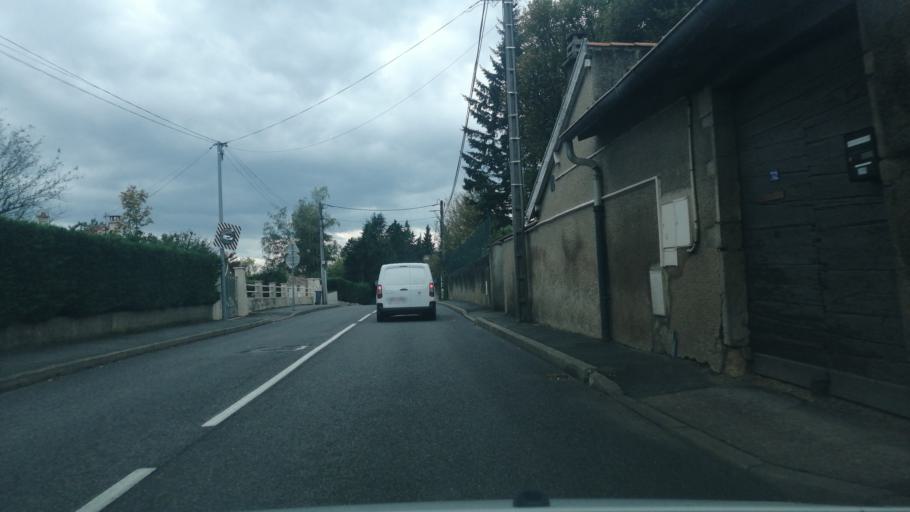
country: FR
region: Rhone-Alpes
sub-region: Departement du Rhone
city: Limonest
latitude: 45.8269
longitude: 4.7676
